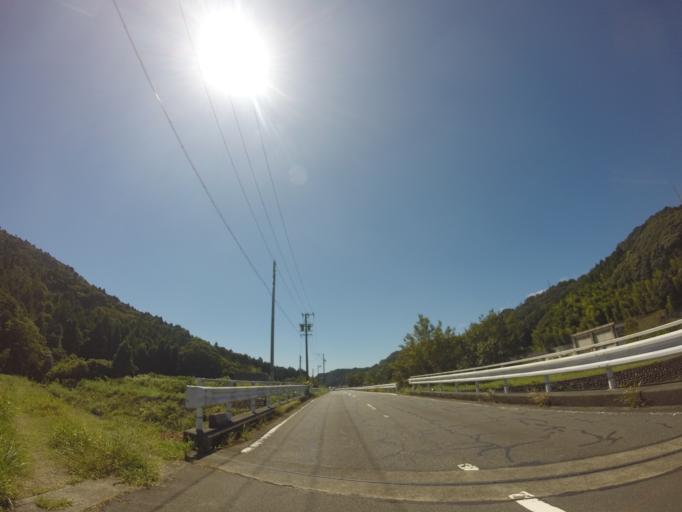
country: JP
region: Shizuoka
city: Kanaya
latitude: 34.8737
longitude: 138.1360
